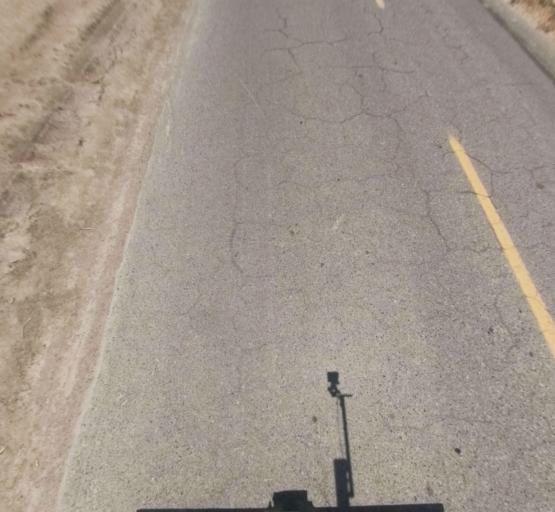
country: US
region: California
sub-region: Fresno County
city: Kerman
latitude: 36.8221
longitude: -120.1888
